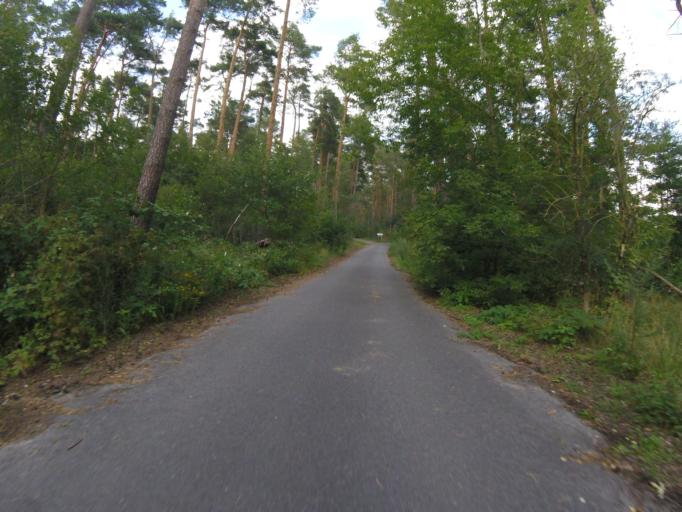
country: DE
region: Brandenburg
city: Halbe
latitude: 52.1092
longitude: 13.7486
